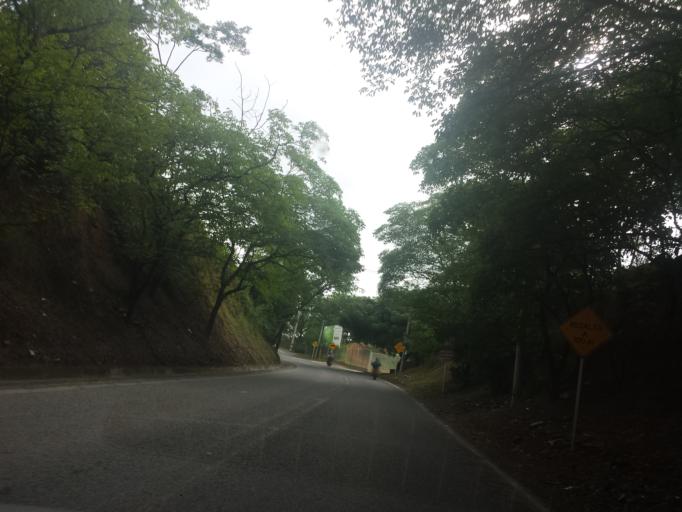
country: CO
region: Antioquia
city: Antioquia
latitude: 6.5517
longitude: -75.8217
